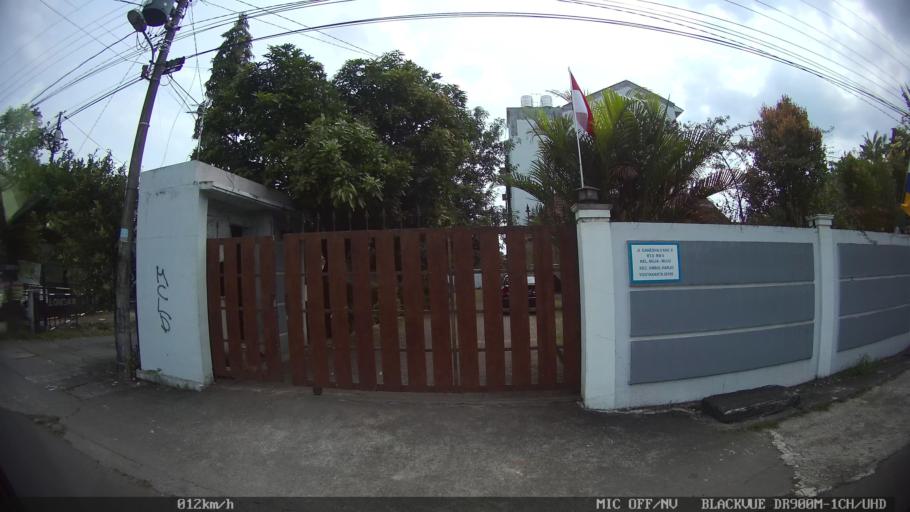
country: ID
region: Daerah Istimewa Yogyakarta
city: Yogyakarta
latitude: -7.7934
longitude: 110.3948
